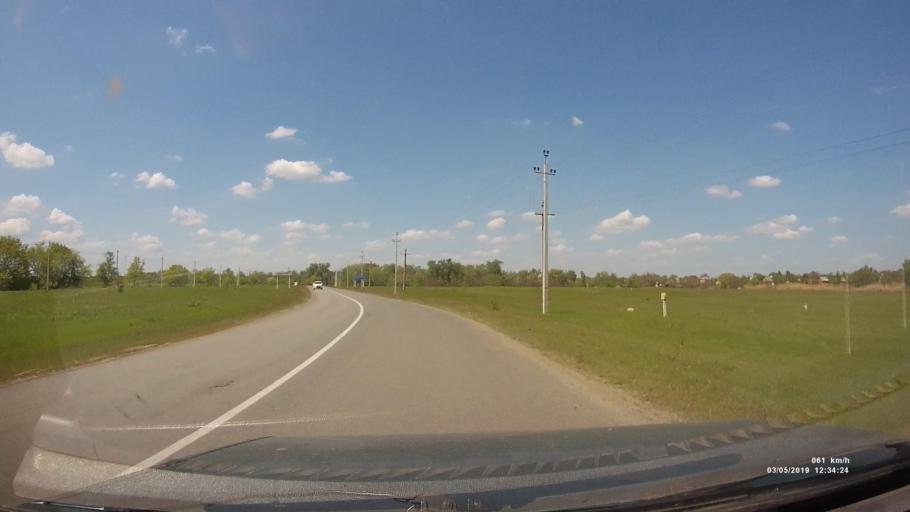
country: RU
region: Rostov
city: Semikarakorsk
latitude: 47.5216
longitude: 40.7685
